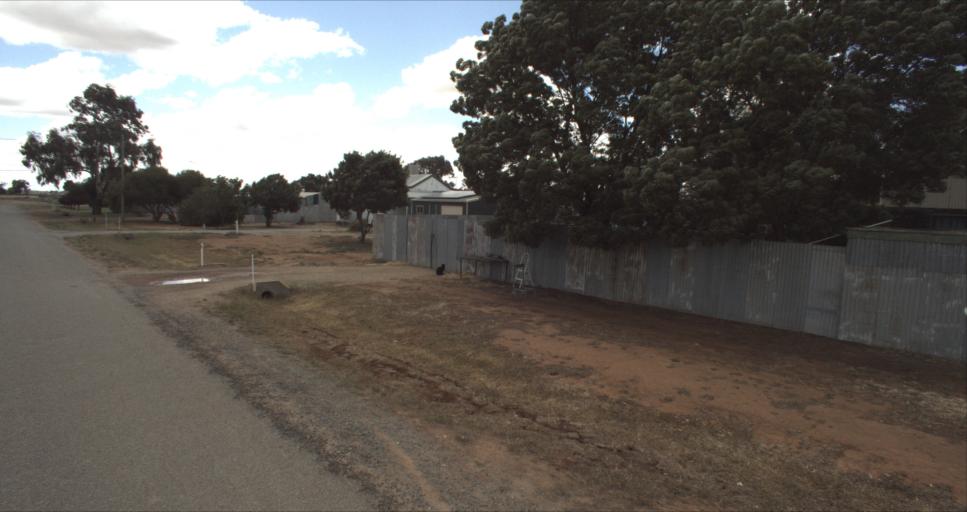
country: AU
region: New South Wales
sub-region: Murrumbidgee Shire
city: Darlington Point
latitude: -34.5153
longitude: 146.1825
